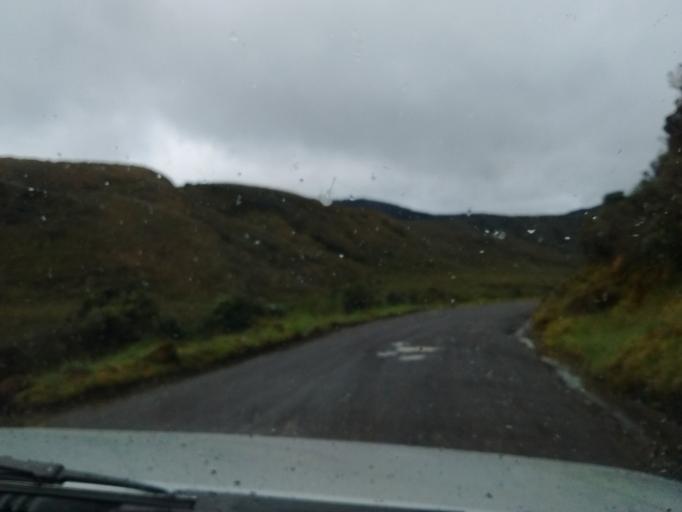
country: CO
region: Cauca
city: Totoro
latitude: 2.3576
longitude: -76.3216
